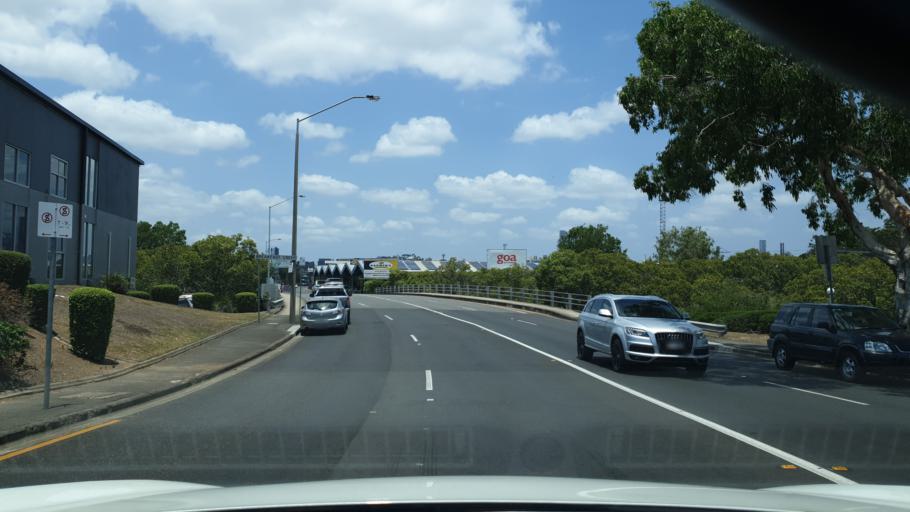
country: AU
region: Queensland
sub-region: Brisbane
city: Wooloowin
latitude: -27.4327
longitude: 153.0406
